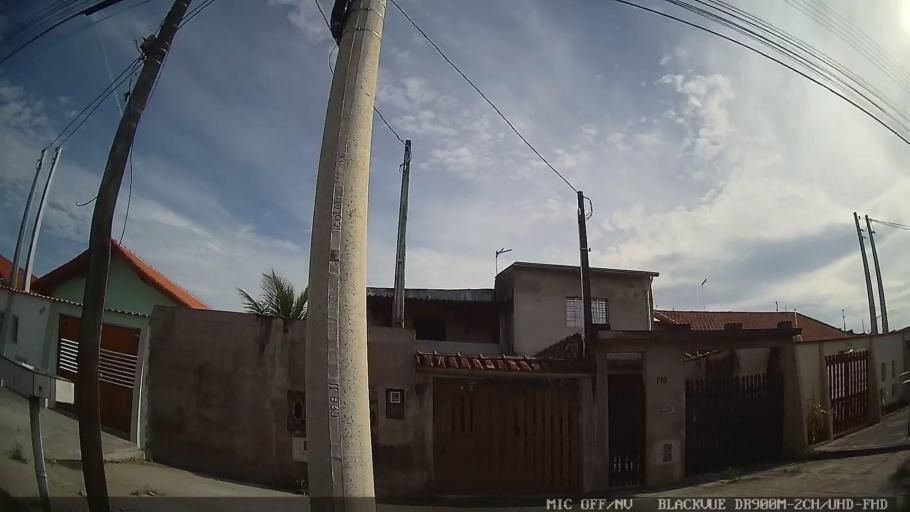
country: BR
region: Sao Paulo
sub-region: Itanhaem
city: Itanhaem
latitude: -24.1620
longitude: -46.7652
